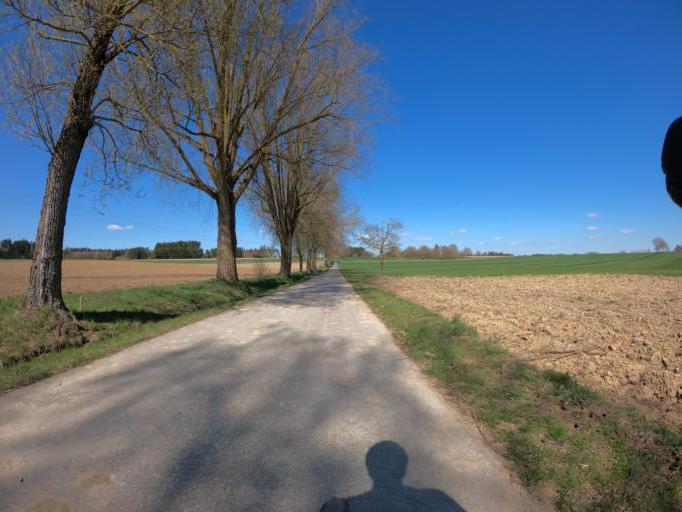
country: DE
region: Baden-Wuerttemberg
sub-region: Karlsruhe Region
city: Empfingen
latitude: 48.4002
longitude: 8.6945
